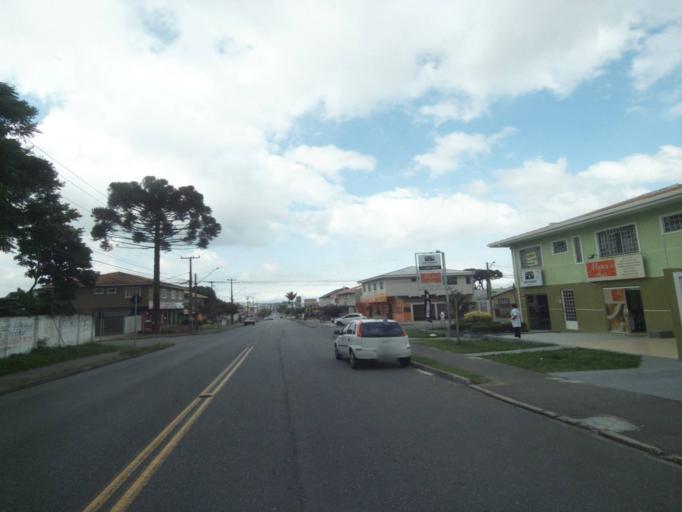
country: BR
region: Parana
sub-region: Pinhais
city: Pinhais
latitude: -25.4518
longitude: -49.2117
